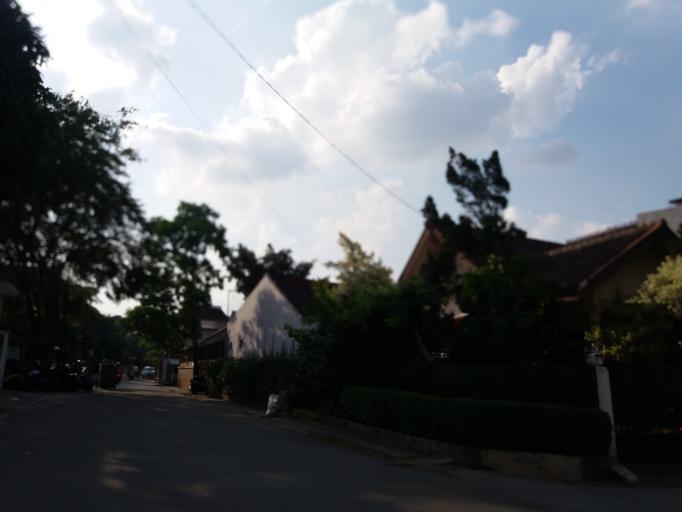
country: ID
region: Jakarta Raya
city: Jakarta
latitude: -6.2466
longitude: 106.8107
